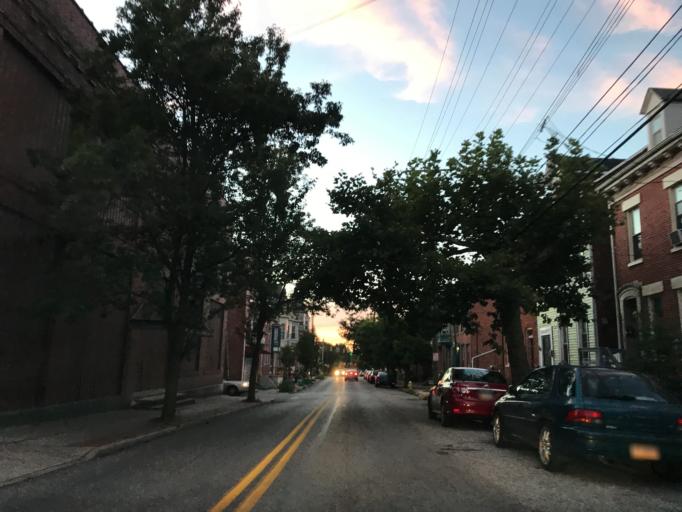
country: US
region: Pennsylvania
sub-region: York County
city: York
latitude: 39.9589
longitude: -76.7303
